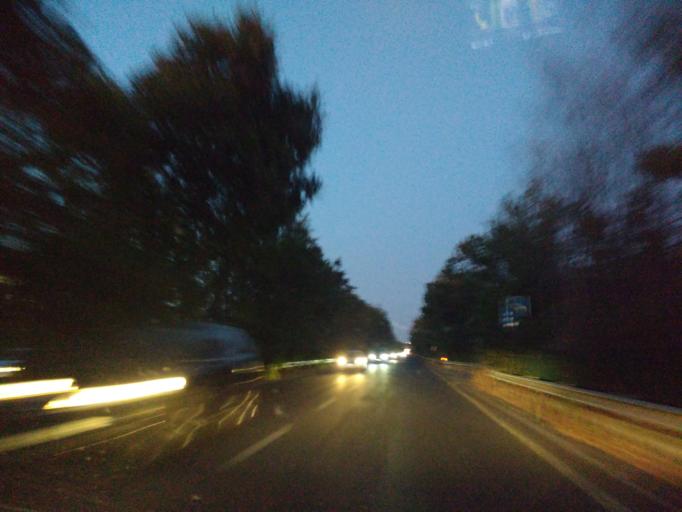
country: IT
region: Latium
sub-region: Citta metropolitana di Roma Capitale
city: Acilia-Castel Fusano-Ostia Antica
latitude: 41.7717
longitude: 12.3292
